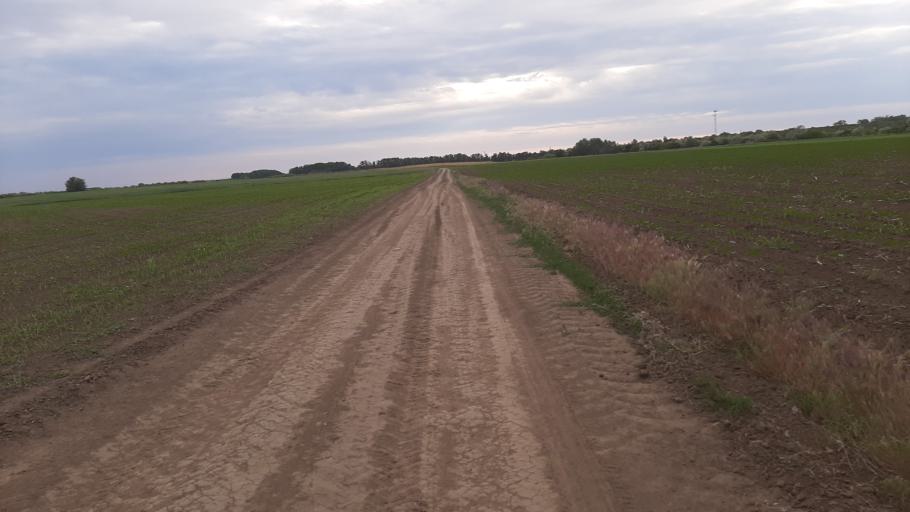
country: HU
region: Csongrad
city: Deszk
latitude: 46.1679
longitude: 20.1909
